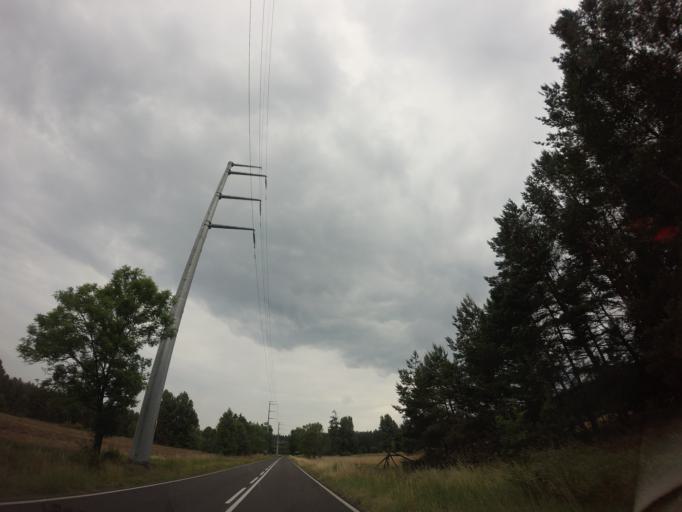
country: PL
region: West Pomeranian Voivodeship
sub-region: Powiat drawski
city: Czaplinek
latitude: 53.4874
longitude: 16.2281
